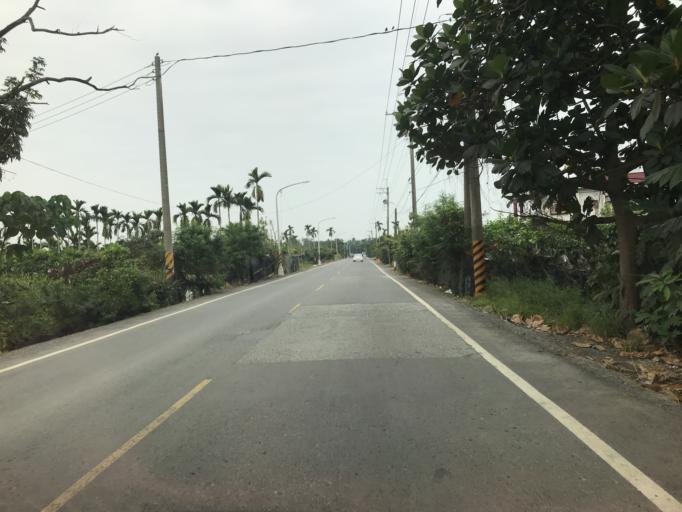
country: TW
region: Taiwan
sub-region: Pingtung
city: Pingtung
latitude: 22.4726
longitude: 120.6073
